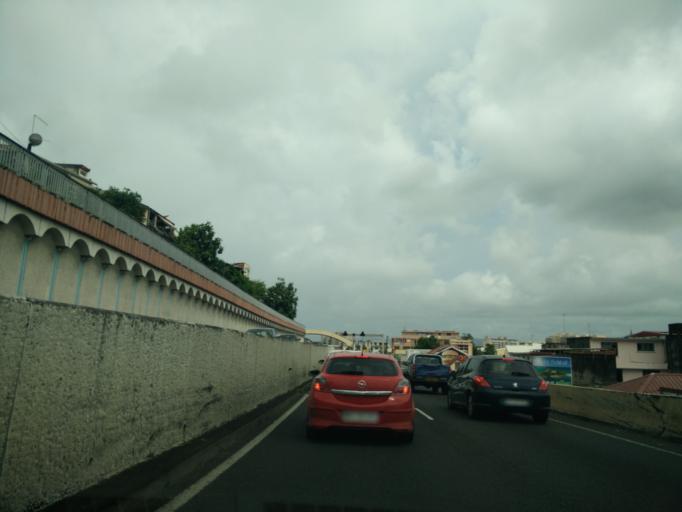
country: MQ
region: Martinique
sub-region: Martinique
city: Fort-de-France
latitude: 14.6123
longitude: -61.0704
